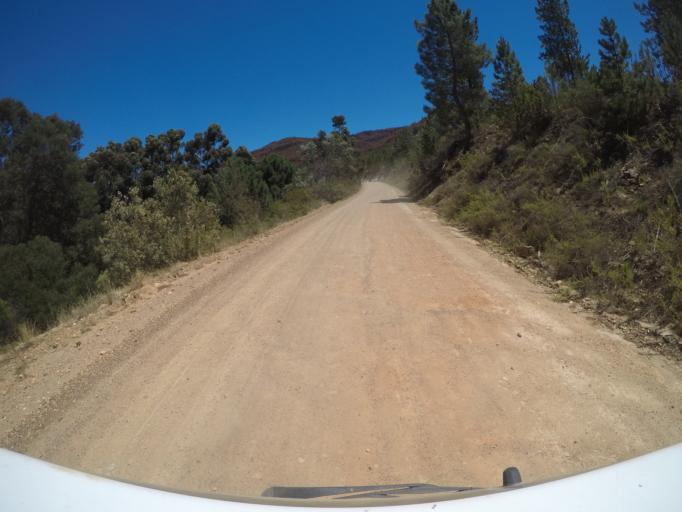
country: ZA
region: Western Cape
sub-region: Overberg District Municipality
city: Caledon
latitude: -34.1586
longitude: 19.2278
